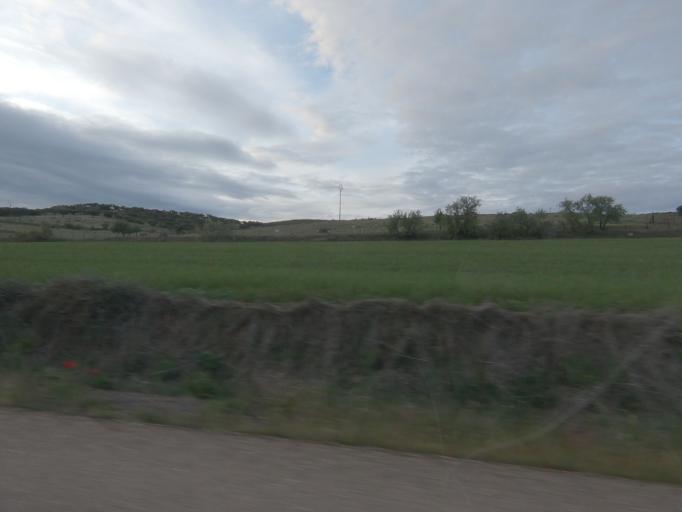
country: ES
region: Extremadura
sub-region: Provincia de Badajoz
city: La Roca de la Sierra
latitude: 39.1088
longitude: -6.7021
